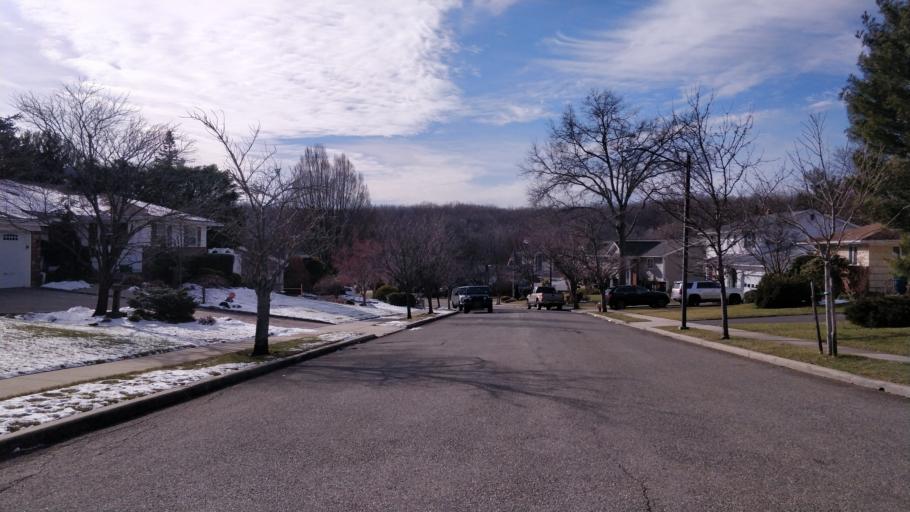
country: US
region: New York
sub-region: Nassau County
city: East Norwich
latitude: 40.8545
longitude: -73.5318
